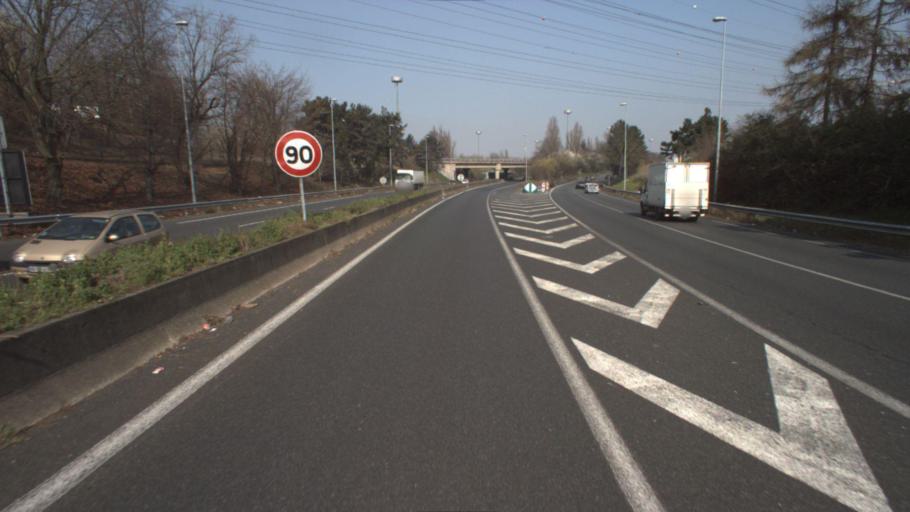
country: FR
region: Ile-de-France
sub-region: Departement du Val-de-Marne
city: Chevilly-Larue
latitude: 48.7632
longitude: 2.3441
